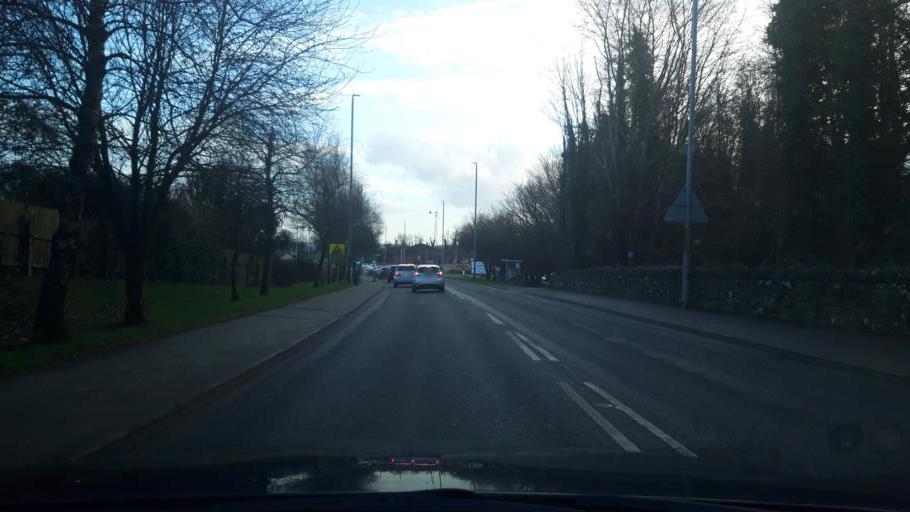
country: GB
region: Northern Ireland
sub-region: Dungannon District
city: Dungannon
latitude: 54.4902
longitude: -6.7485
